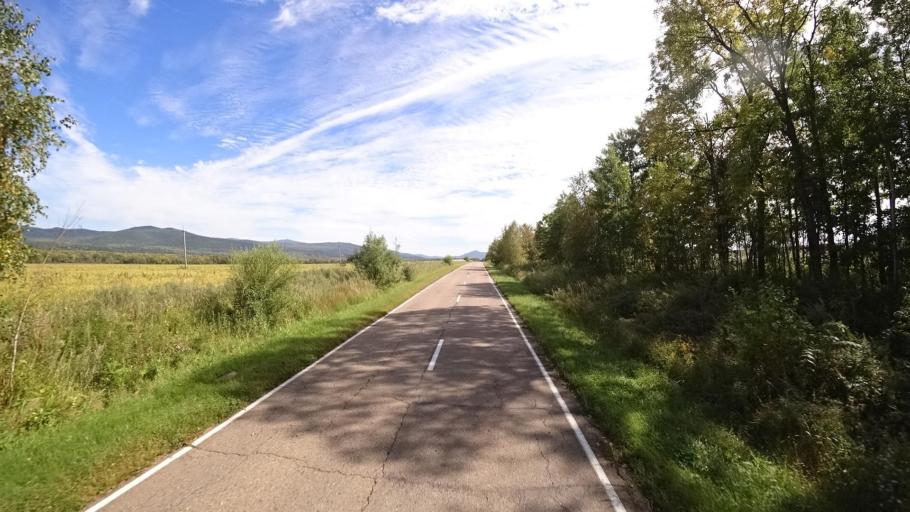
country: RU
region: Primorskiy
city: Yakovlevka
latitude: 44.4183
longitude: 133.5817
